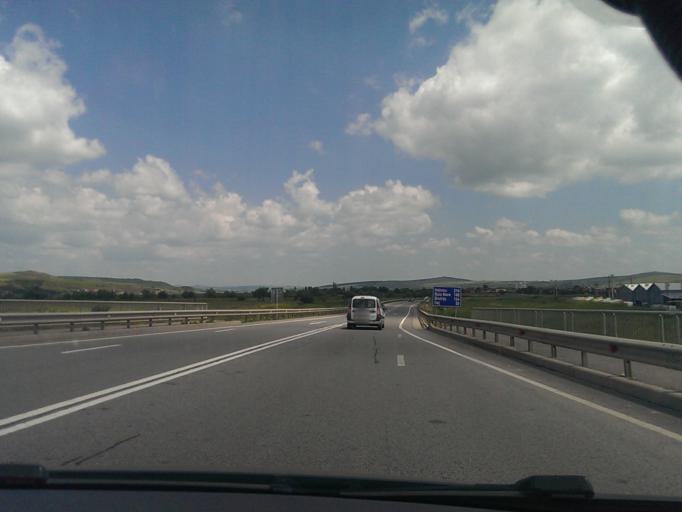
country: RO
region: Cluj
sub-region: Comuna Apahida
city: Sannicoara
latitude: 46.7838
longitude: 23.7060
